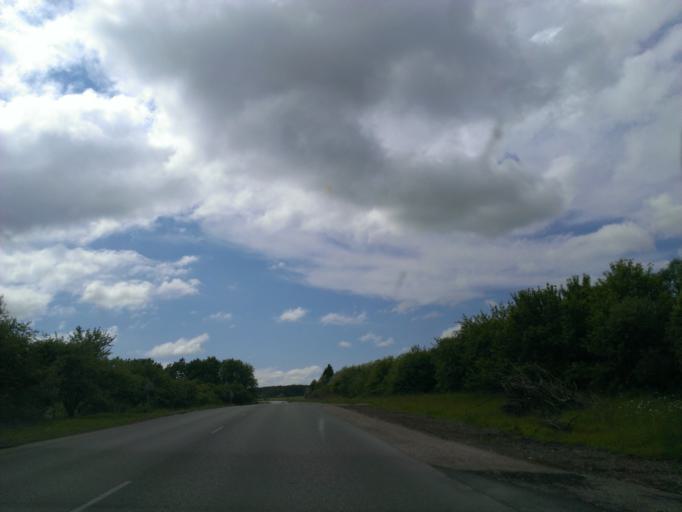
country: LV
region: Durbe
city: Liegi
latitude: 56.5827
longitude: 21.3344
